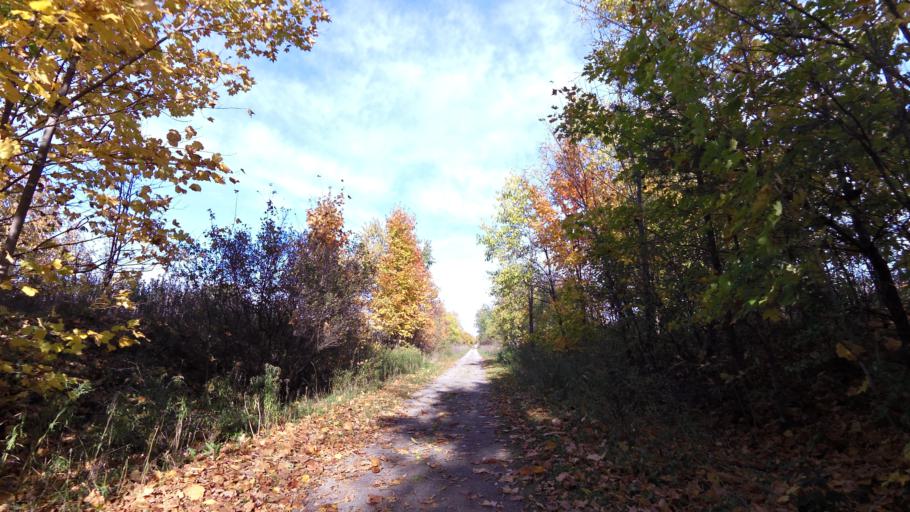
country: CA
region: Ontario
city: Orangeville
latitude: 43.7984
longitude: -80.0406
